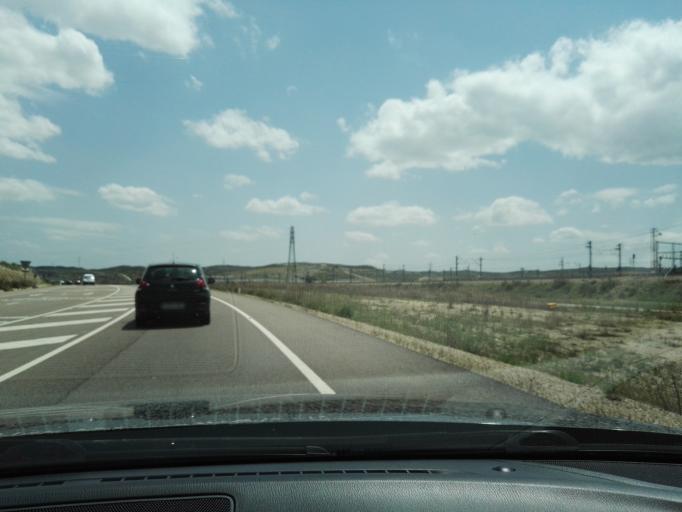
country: ES
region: Aragon
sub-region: Provincia de Zaragoza
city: Montecanal
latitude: 41.6266
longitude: -0.9894
